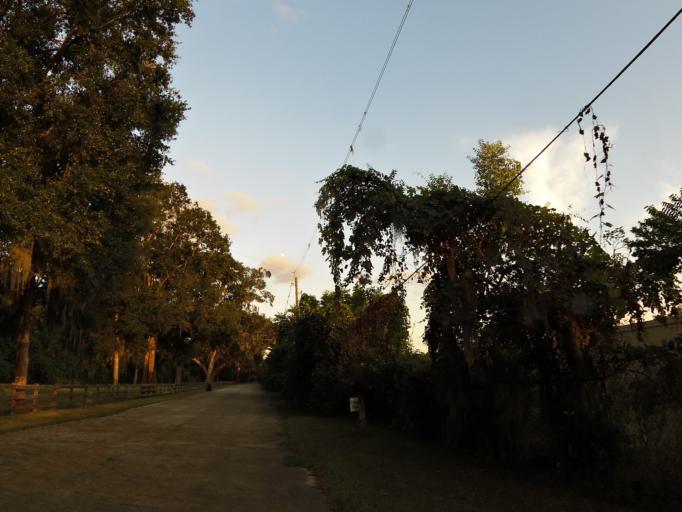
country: US
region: Florida
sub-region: Clay County
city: Orange Park
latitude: 30.1860
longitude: -81.6387
